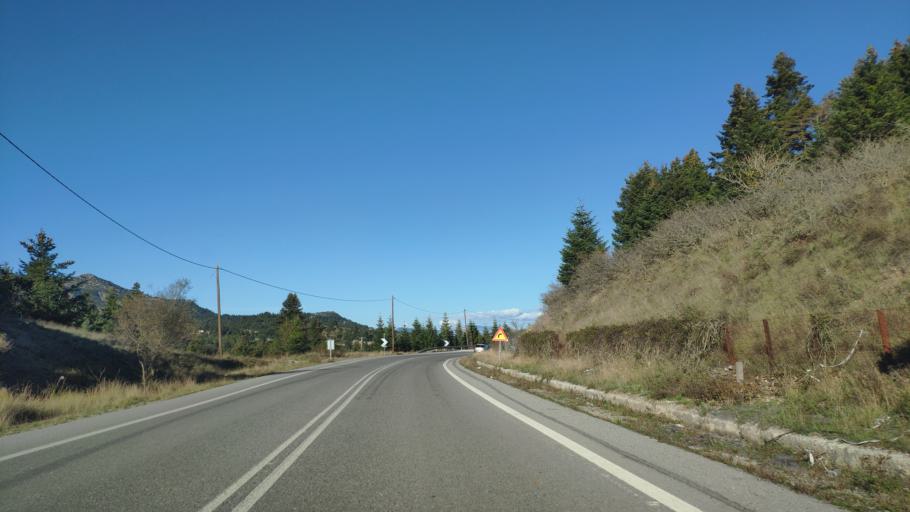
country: GR
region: Peloponnese
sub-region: Nomos Arkadias
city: Langadhia
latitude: 37.6555
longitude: 22.1261
